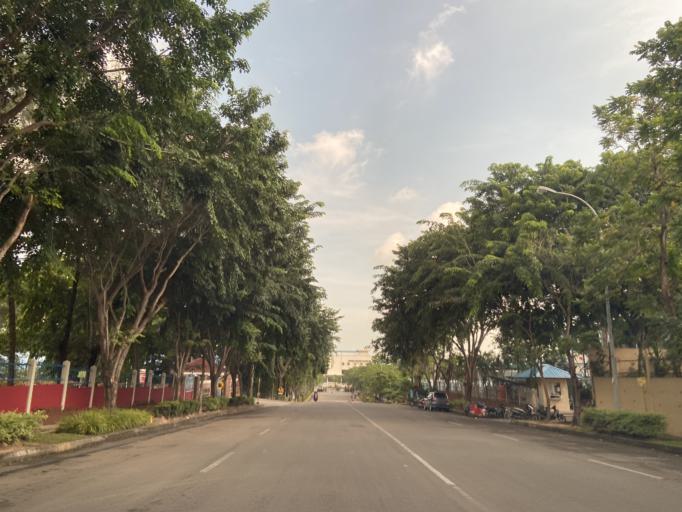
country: SG
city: Singapore
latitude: 1.1088
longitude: 104.0722
